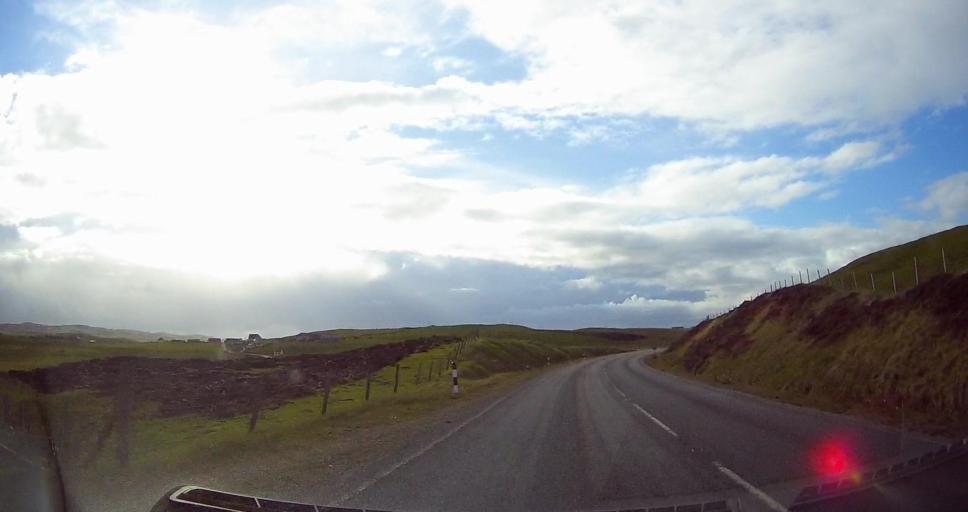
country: GB
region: Scotland
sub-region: Shetland Islands
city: Lerwick
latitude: 60.3717
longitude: -1.3338
